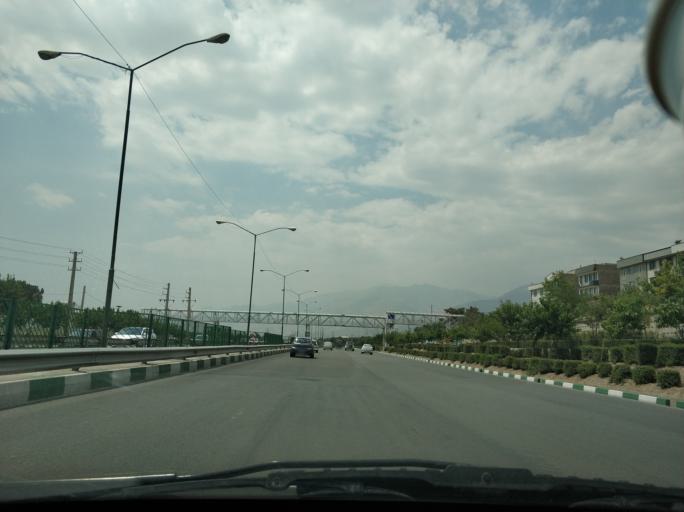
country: IR
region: Tehran
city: Tajrish
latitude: 35.7664
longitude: 51.5631
